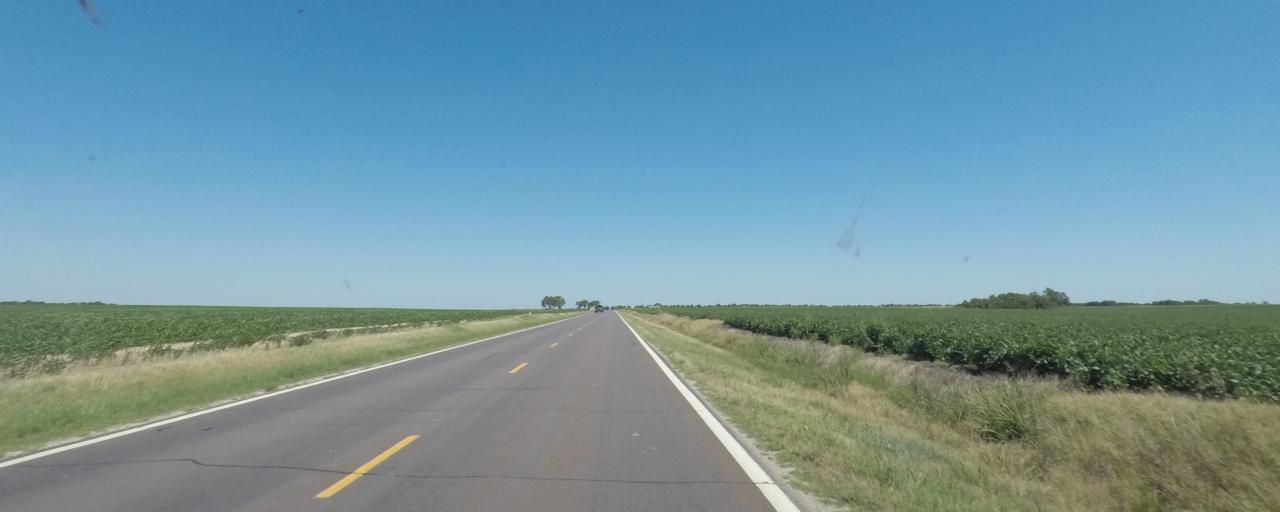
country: US
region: Kansas
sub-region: Sumner County
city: Wellington
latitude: 37.1664
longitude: -97.4021
